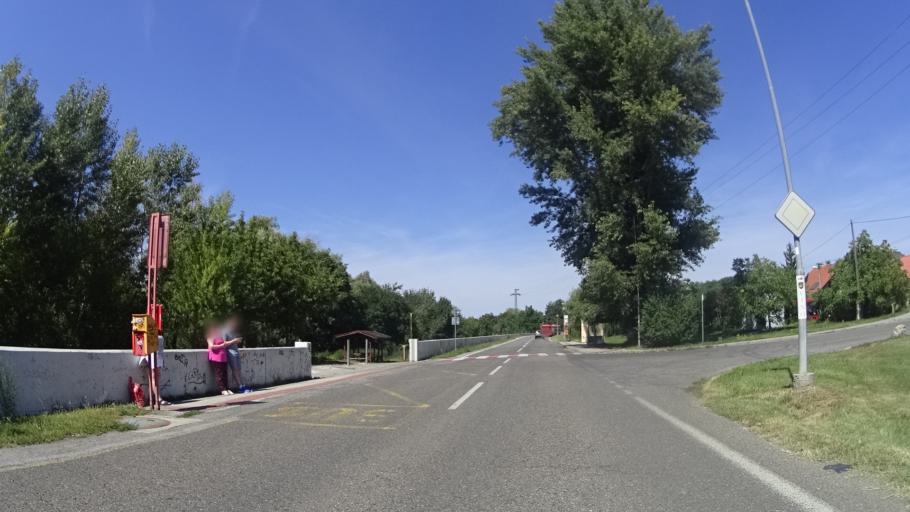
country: AT
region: Lower Austria
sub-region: Politischer Bezirk Bruck an der Leitha
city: Hainburg an der Donau
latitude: 48.2043
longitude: 16.9704
